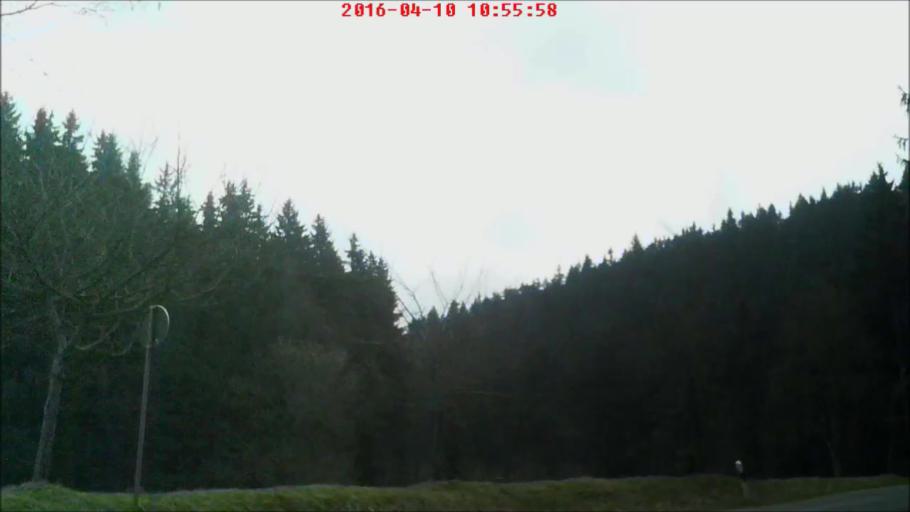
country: DE
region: Thuringia
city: Stutzerbach
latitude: 50.6236
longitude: 10.8554
